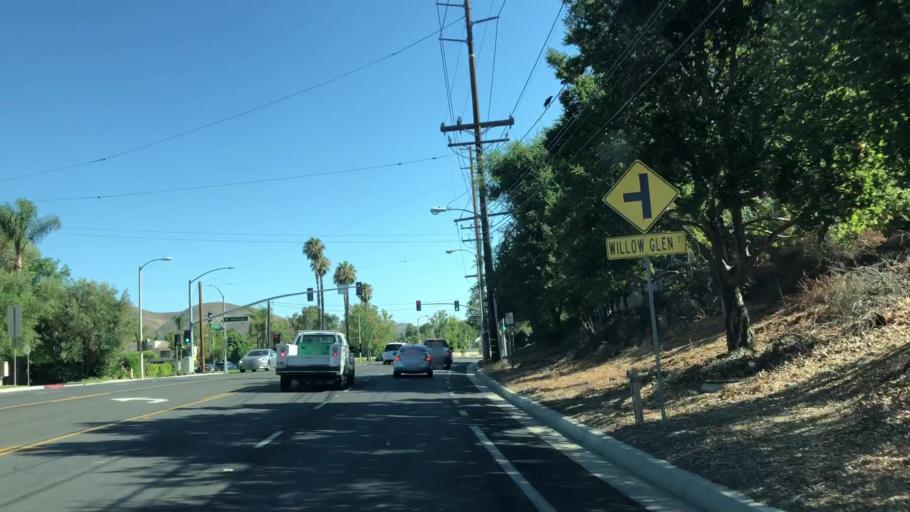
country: US
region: California
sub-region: Los Angeles County
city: Agoura
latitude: 34.1357
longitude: -118.7025
